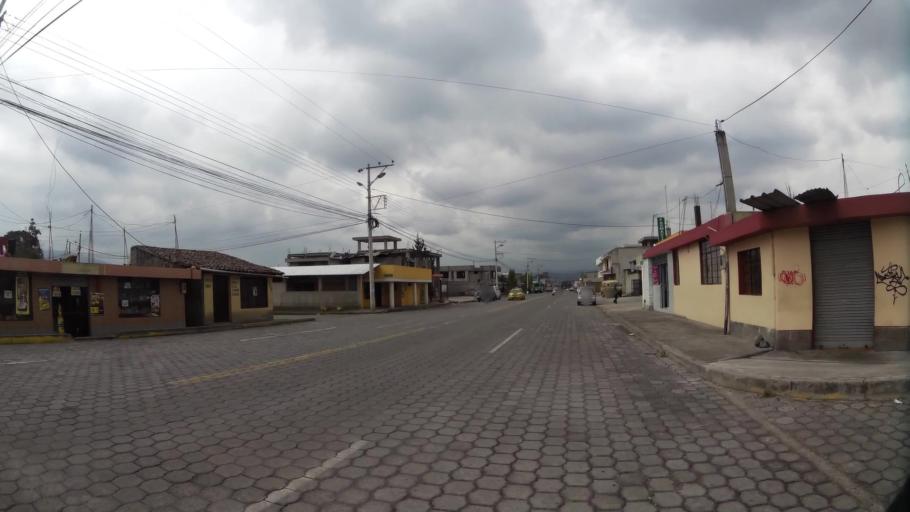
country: EC
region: Pichincha
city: Sangolqui
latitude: -0.3271
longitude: -78.4743
